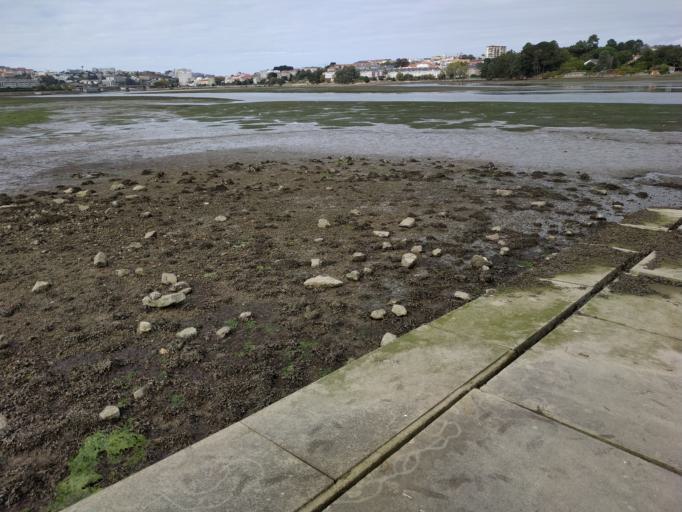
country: ES
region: Galicia
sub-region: Provincia da Coruna
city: Cambre
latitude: 43.3216
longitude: -8.3703
